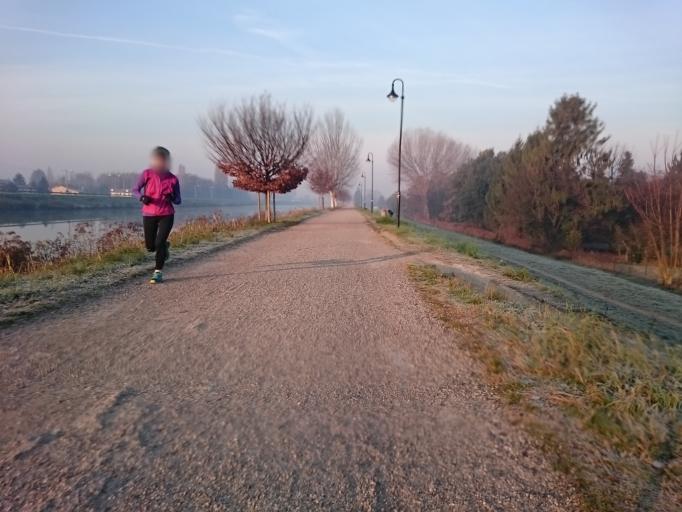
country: IT
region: Veneto
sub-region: Provincia di Padova
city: Padova
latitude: 45.3847
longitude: 11.8926
